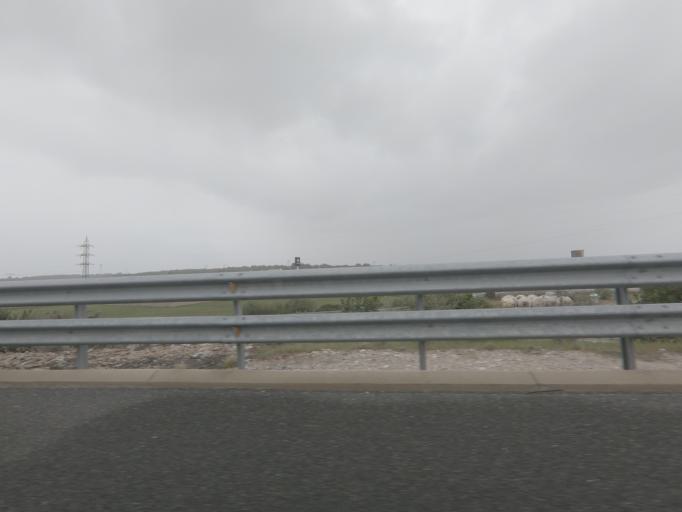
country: ES
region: Extremadura
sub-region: Provincia de Caceres
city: Villar de Plasencia
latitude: 40.1426
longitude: -6.0406
